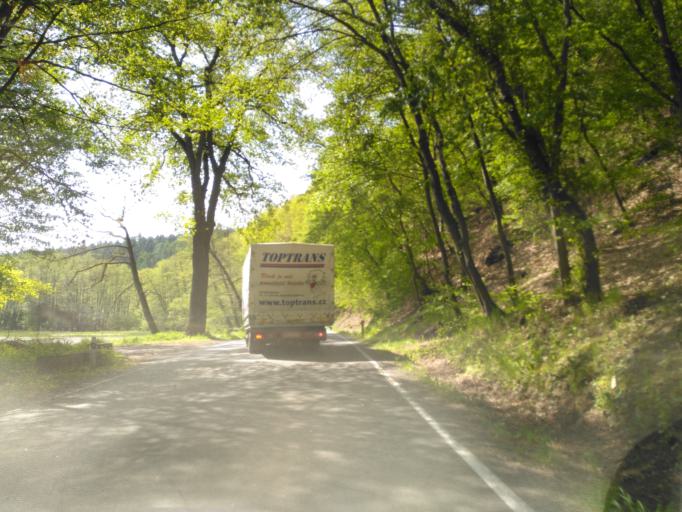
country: CZ
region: Central Bohemia
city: Lochovice
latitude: 49.8312
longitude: 13.9654
